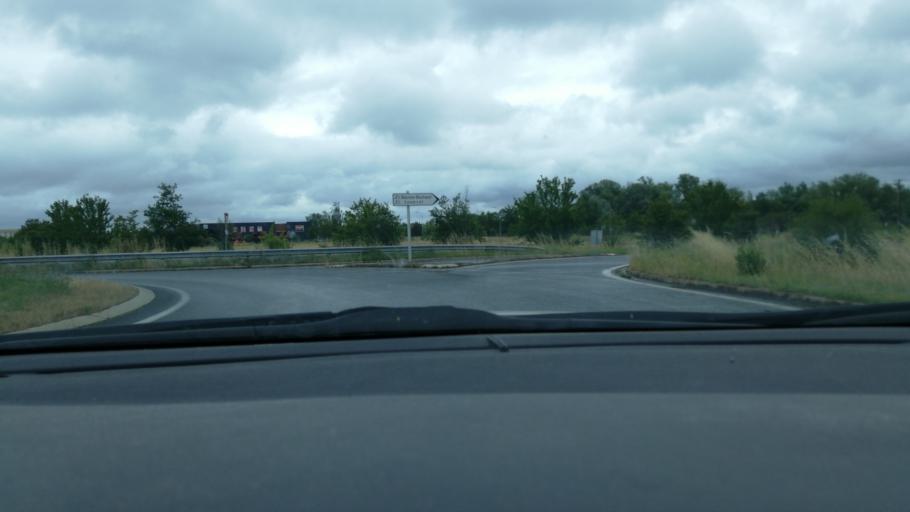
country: FR
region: Poitou-Charentes
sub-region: Departement de la Vienne
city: Naintre
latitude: 46.7477
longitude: 0.4767
